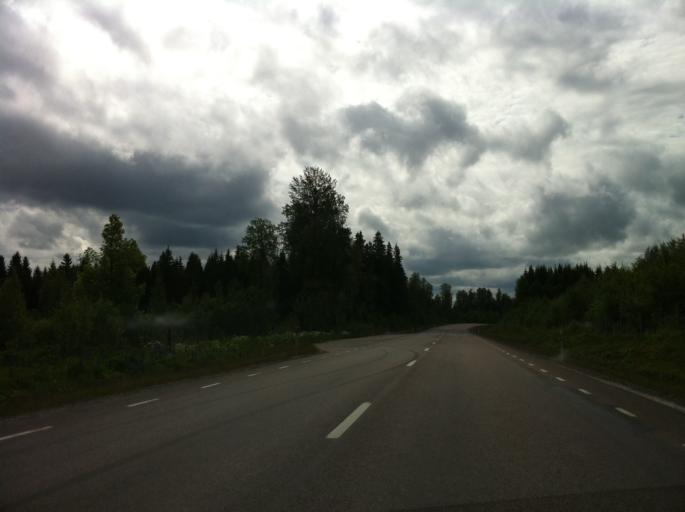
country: SE
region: Vaermland
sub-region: Sunne Kommun
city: Sunne
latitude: 59.7461
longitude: 13.1252
